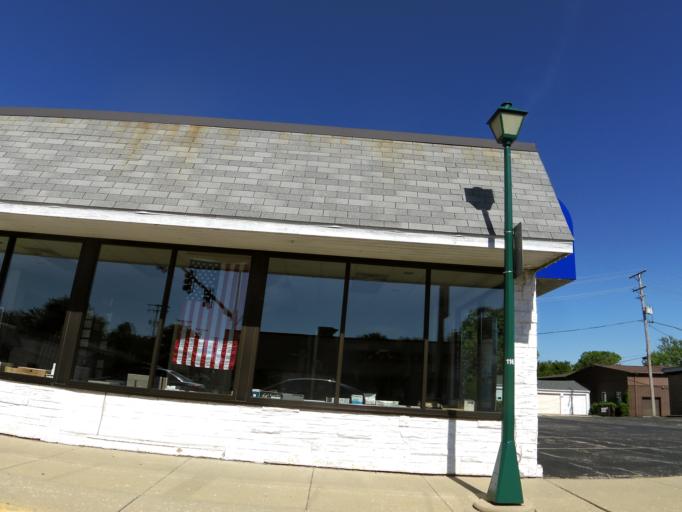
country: US
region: Illinois
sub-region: Winnebago County
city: Loves Park
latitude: 42.3122
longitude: -89.0577
